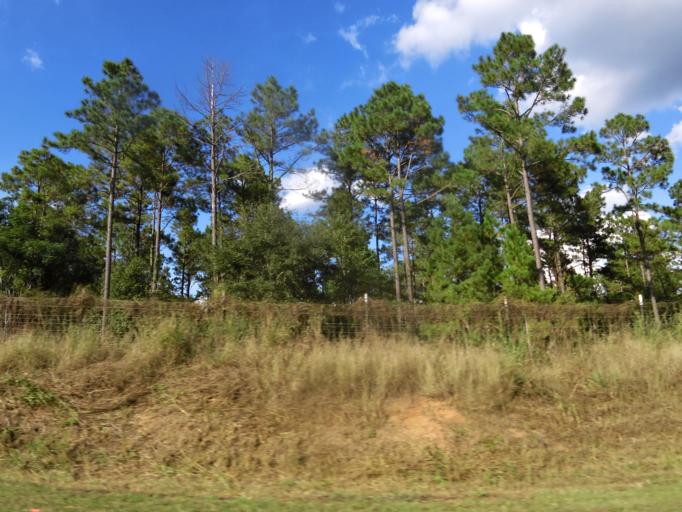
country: US
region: Georgia
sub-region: Brooks County
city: Quitman
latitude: 30.7783
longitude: -83.6142
